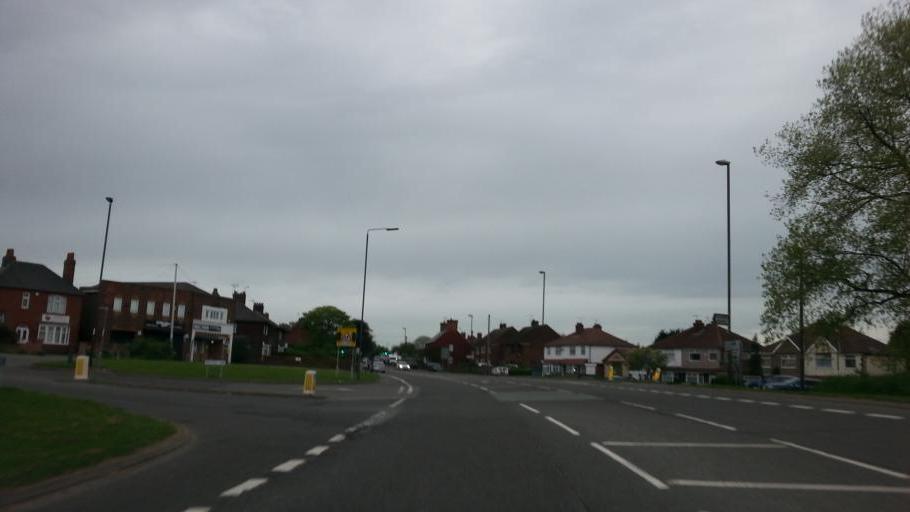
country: GB
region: England
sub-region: Derbyshire
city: Pinxton
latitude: 53.1013
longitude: -1.3289
